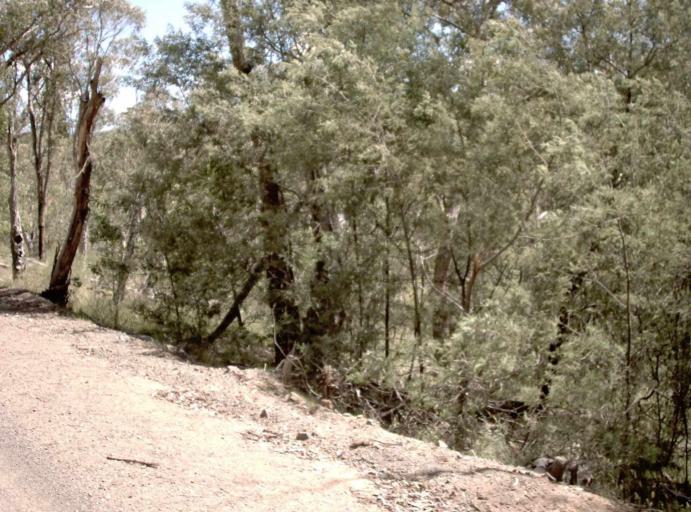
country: AU
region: New South Wales
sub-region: Bombala
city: Bombala
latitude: -37.1365
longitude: 148.6612
